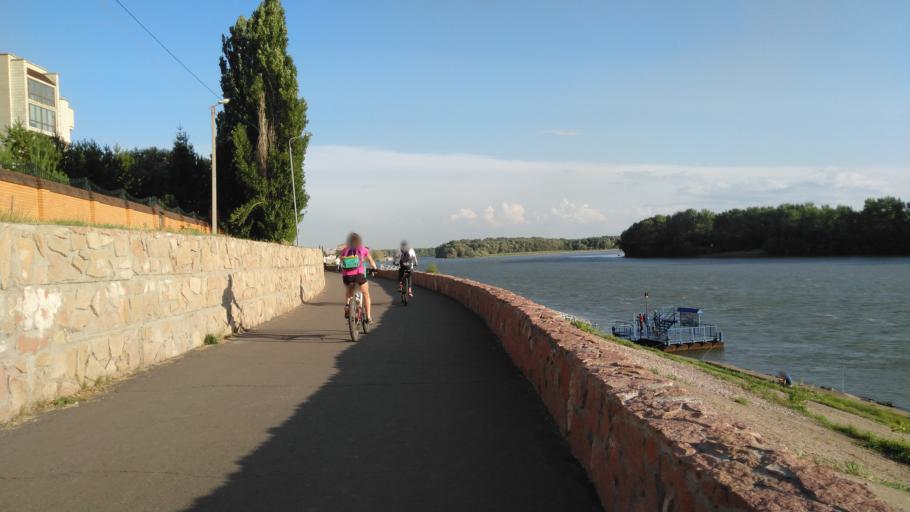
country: KZ
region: Pavlodar
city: Pavlodar
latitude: 52.2775
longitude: 76.9332
